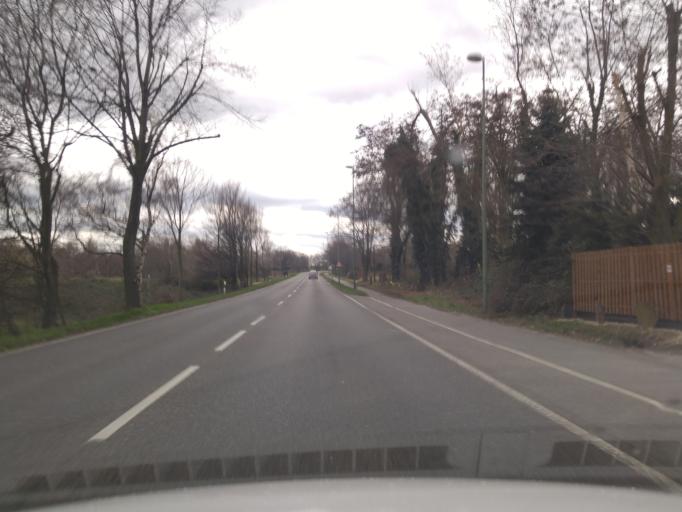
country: DE
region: North Rhine-Westphalia
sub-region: Regierungsbezirk Dusseldorf
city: Dusseldorf
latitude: 51.1531
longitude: 6.7850
